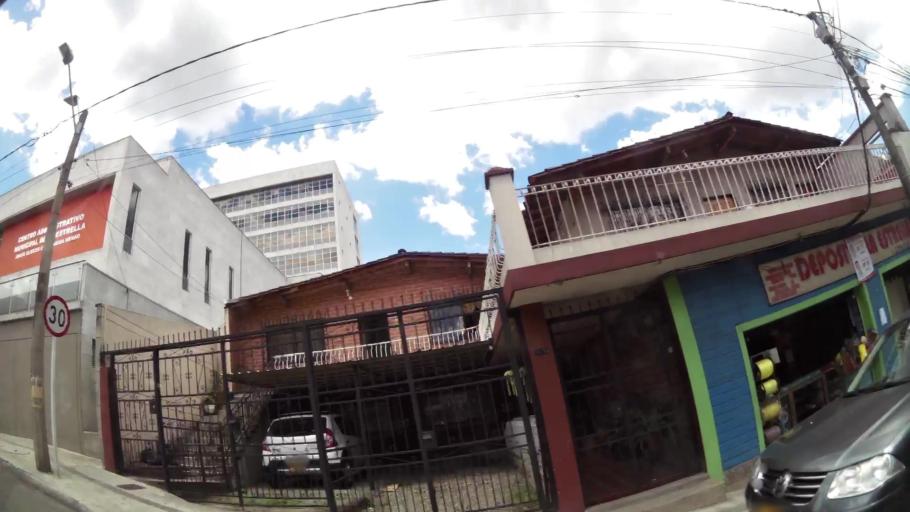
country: CO
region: Antioquia
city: La Estrella
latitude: 6.1575
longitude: -75.6416
